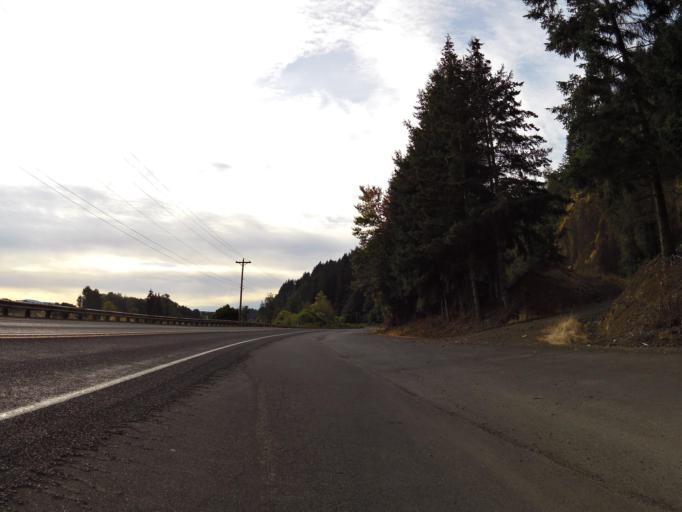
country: US
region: Washington
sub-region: Cowlitz County
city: West Longview
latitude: 46.1875
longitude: -123.0886
